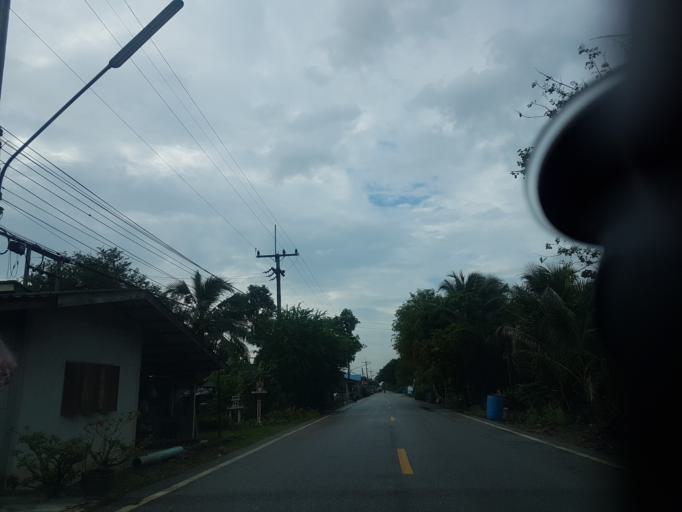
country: TH
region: Pathum Thani
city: Nong Suea
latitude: 14.1507
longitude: 100.8686
